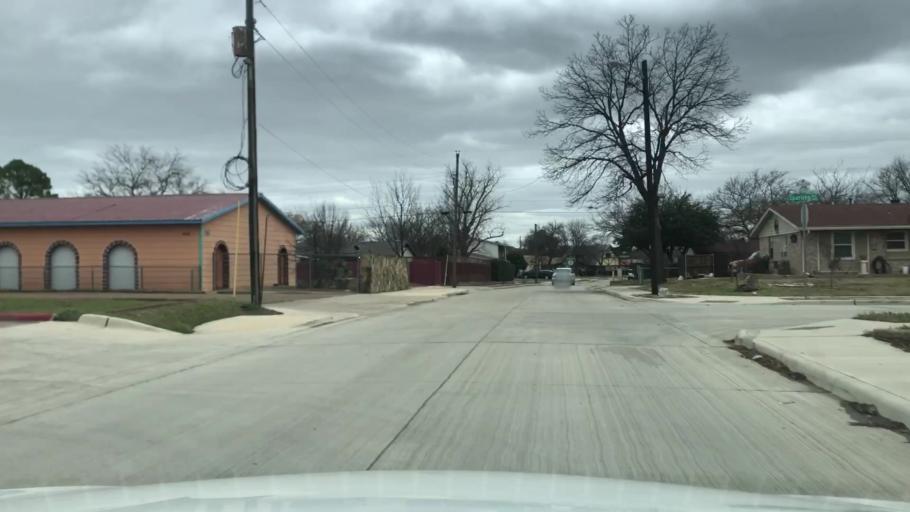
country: US
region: Texas
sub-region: Dallas County
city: Carrollton
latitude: 32.9533
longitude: -96.8727
